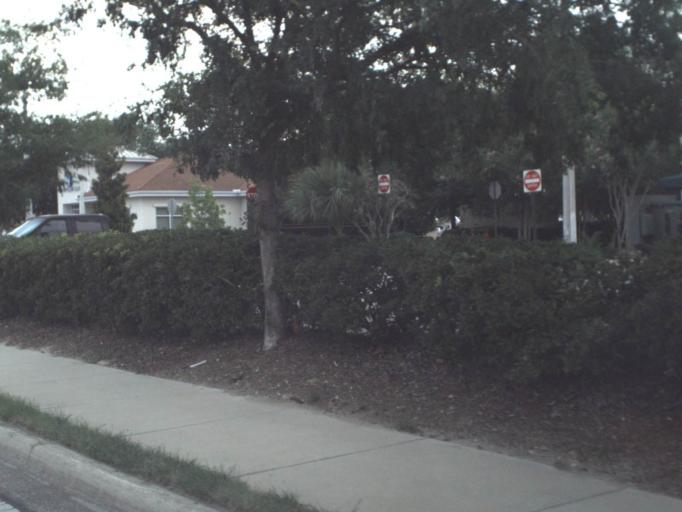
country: US
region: Florida
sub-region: Duval County
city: Jacksonville
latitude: 30.3175
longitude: -81.5574
